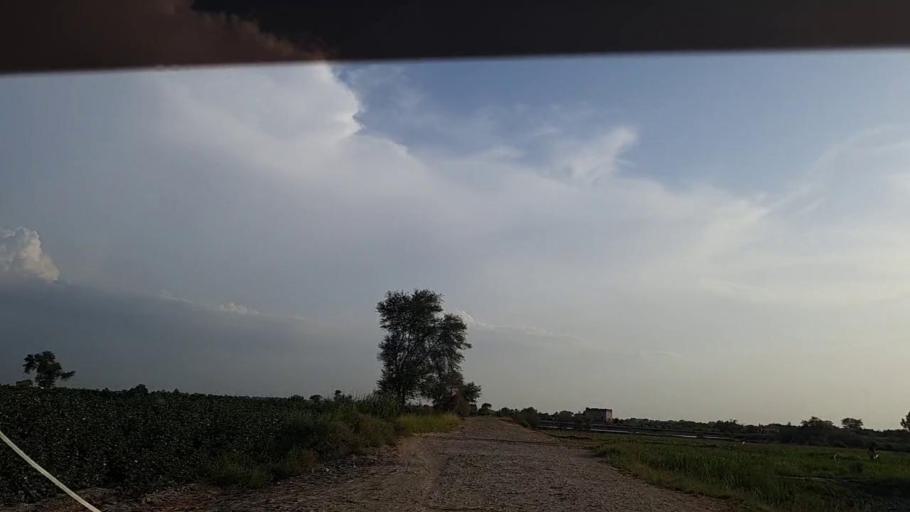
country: PK
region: Sindh
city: Khanpur
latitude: 27.8027
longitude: 69.3139
